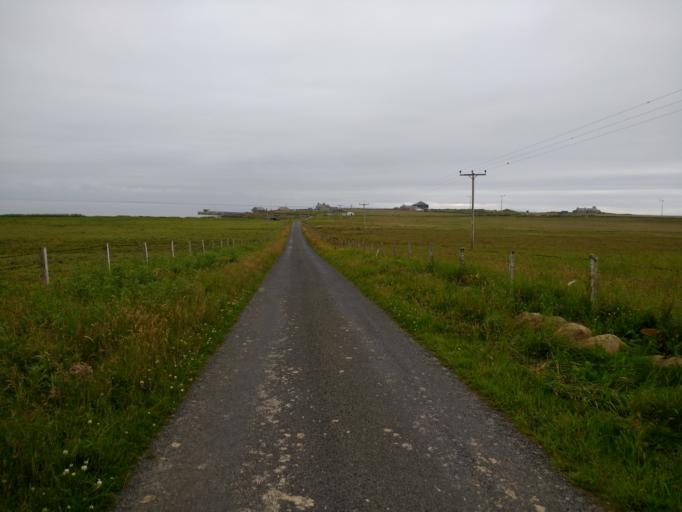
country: GB
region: Scotland
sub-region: Orkney Islands
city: Kirkwall
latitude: 59.3610
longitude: -2.4355
